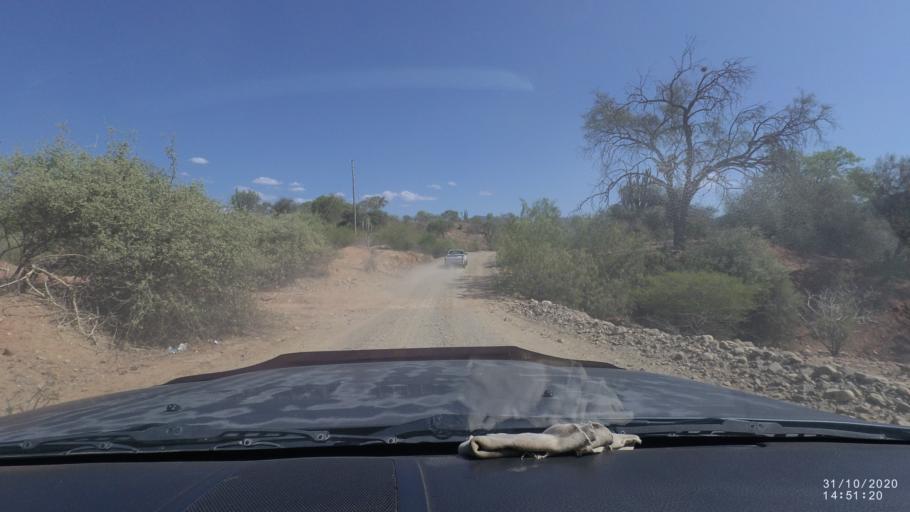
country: BO
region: Cochabamba
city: Aiquile
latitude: -18.2066
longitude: -64.8573
